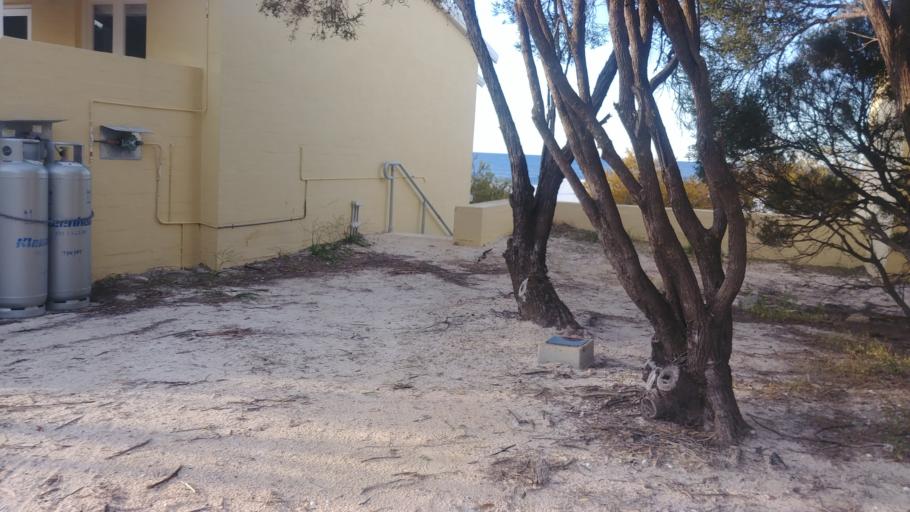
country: AU
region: Western Australia
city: Mosman Park
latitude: -31.9907
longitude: 115.5274
